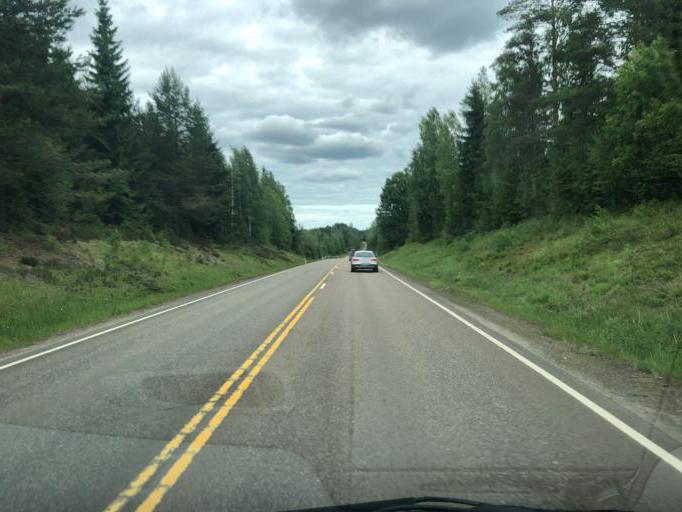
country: FI
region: Kymenlaakso
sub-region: Kouvola
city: Kouvola
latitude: 61.0547
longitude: 27.0365
